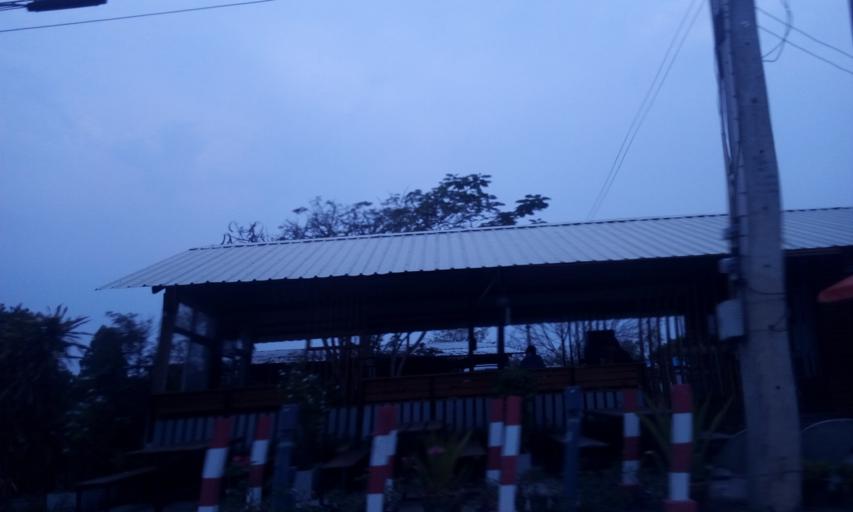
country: TH
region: Chon Buri
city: Ko Chan
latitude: 13.4825
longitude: 101.2797
